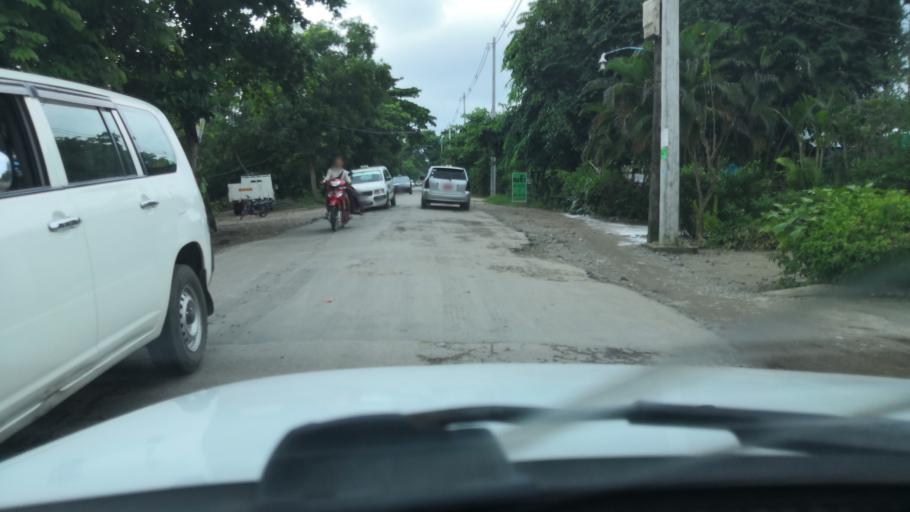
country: MM
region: Yangon
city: Yangon
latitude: 16.8817
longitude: 96.1791
